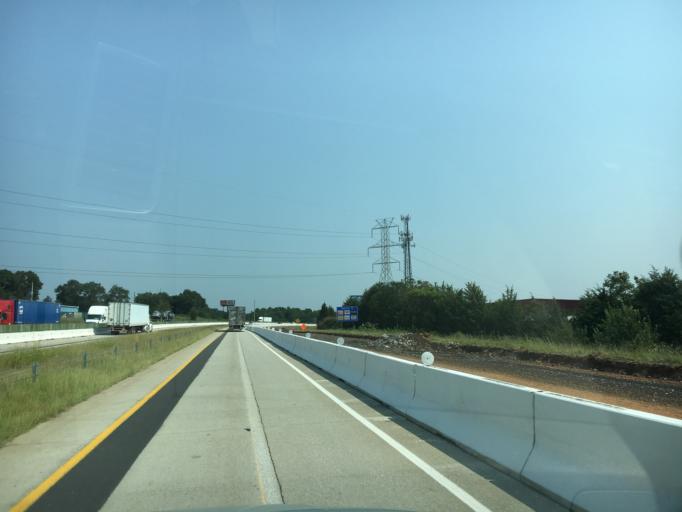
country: US
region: South Carolina
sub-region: Spartanburg County
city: Valley Falls
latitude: 35.0097
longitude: -81.9794
